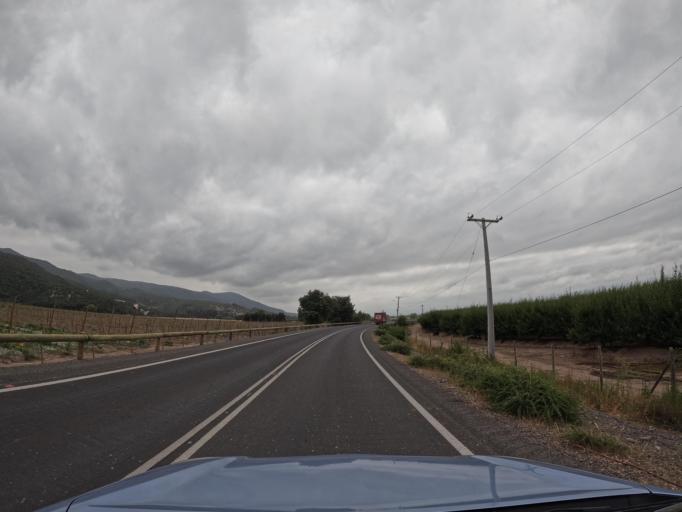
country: CL
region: O'Higgins
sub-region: Provincia de Colchagua
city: Chimbarongo
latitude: -34.7235
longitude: -71.0903
